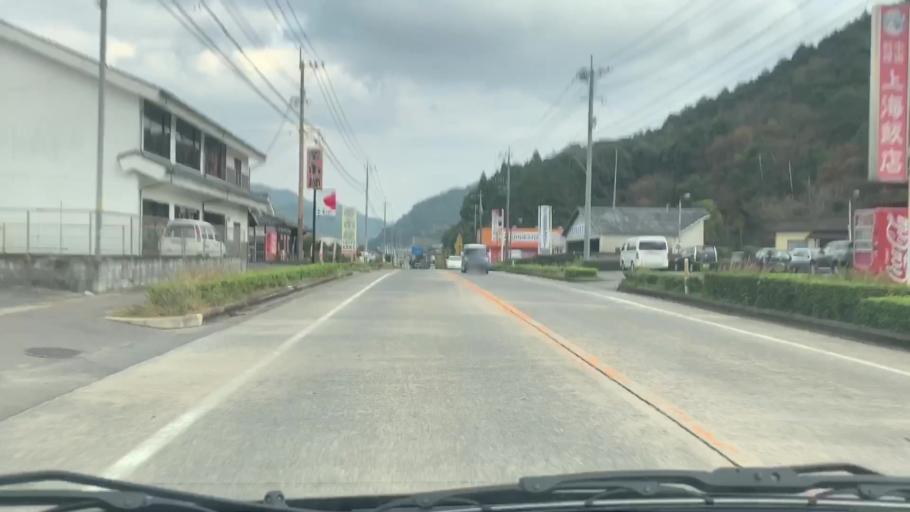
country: JP
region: Saga Prefecture
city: Imaricho-ko
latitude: 33.1838
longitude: 129.8731
